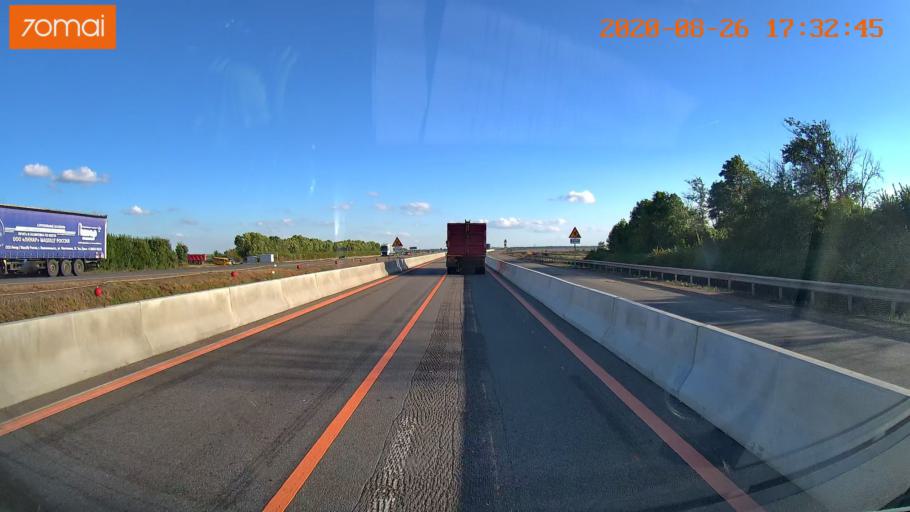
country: RU
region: Tula
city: Kazachka
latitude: 53.4184
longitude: 38.1815
